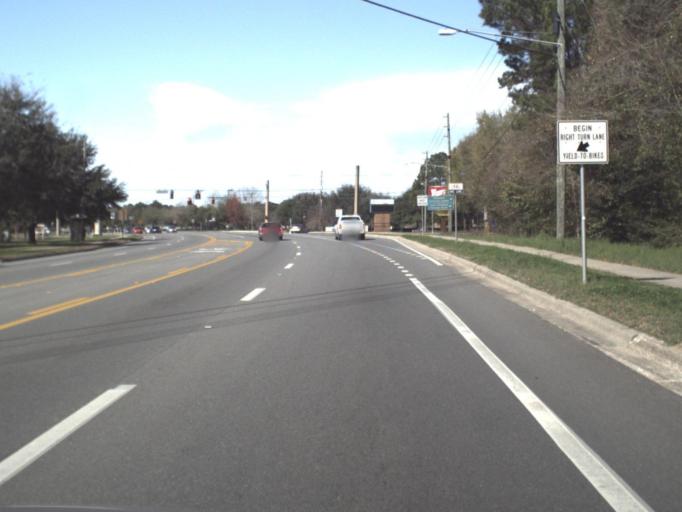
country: US
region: Florida
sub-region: Leon County
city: Tallahassee
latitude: 30.4416
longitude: -84.3361
